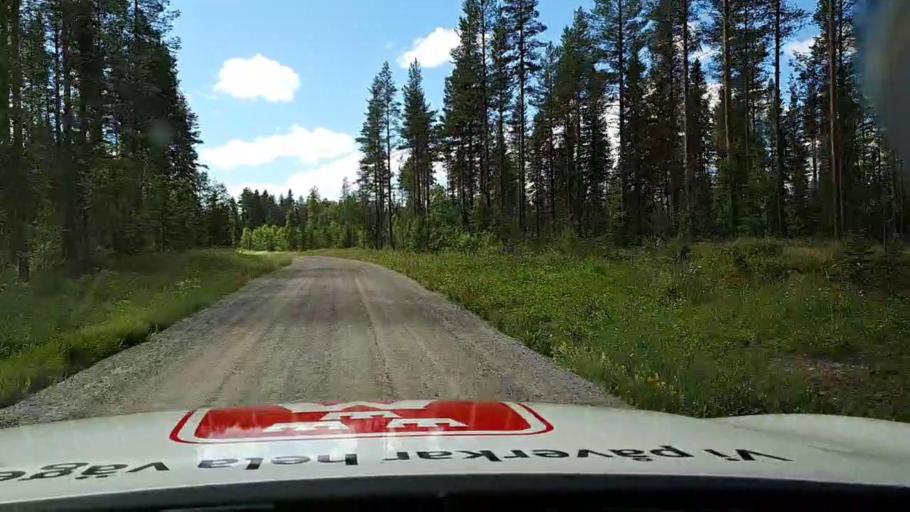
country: SE
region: Jaemtland
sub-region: Braecke Kommun
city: Braecke
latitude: 62.7475
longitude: 15.5024
